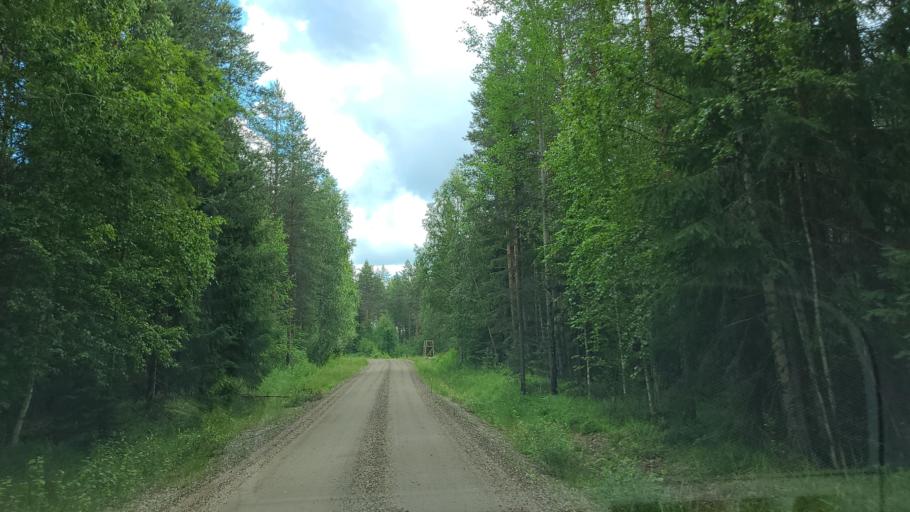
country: FI
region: Northern Savo
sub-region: Koillis-Savo
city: Kaavi
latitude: 63.0356
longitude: 28.7930
